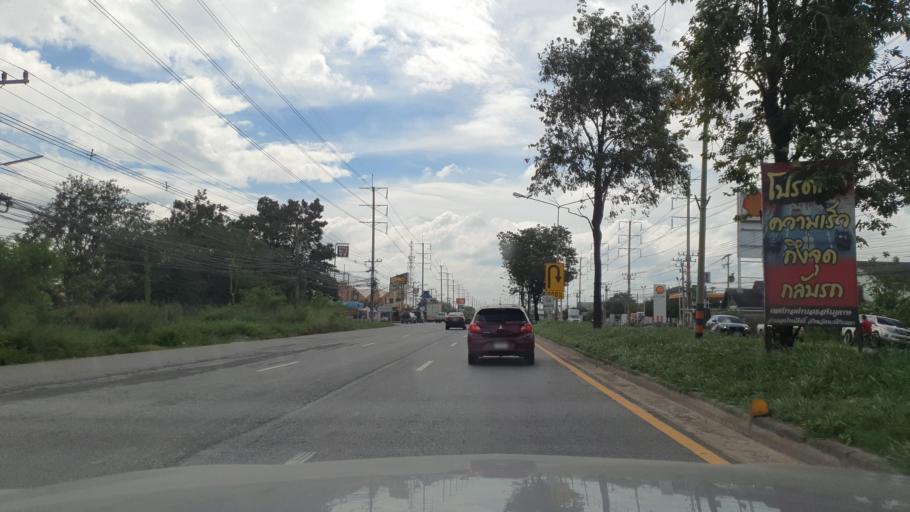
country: TH
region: Chachoengsao
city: Bang Pakong
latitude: 13.5814
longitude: 101.0078
